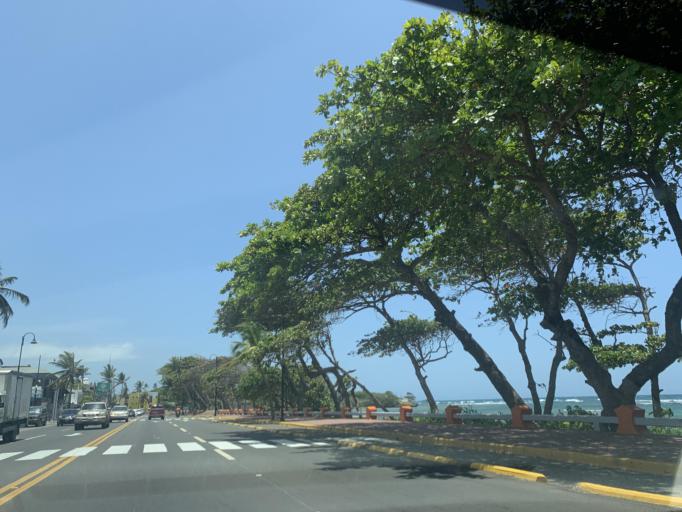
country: DO
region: Puerto Plata
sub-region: Puerto Plata
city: Puerto Plata
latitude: 19.7996
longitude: -70.6906
